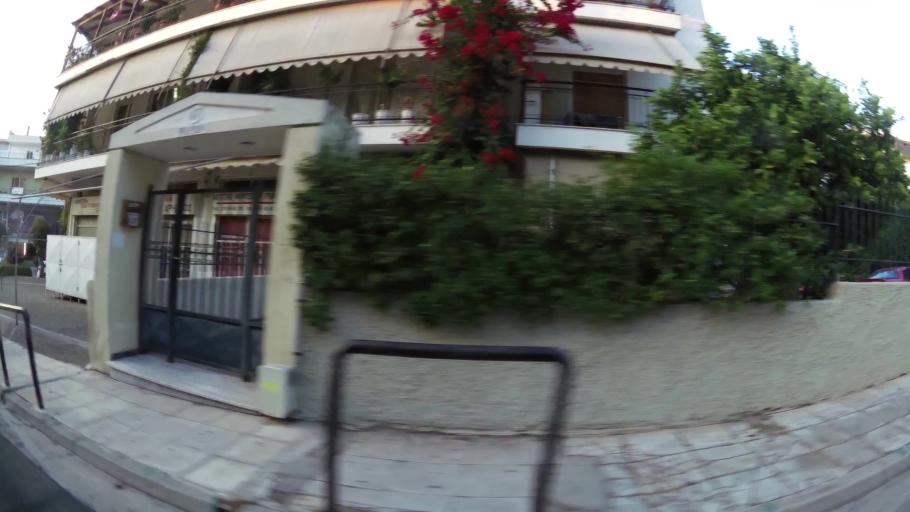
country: GR
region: Attica
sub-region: Nomarchia Athinas
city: Agia Paraskevi
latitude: 38.0144
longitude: 23.8326
